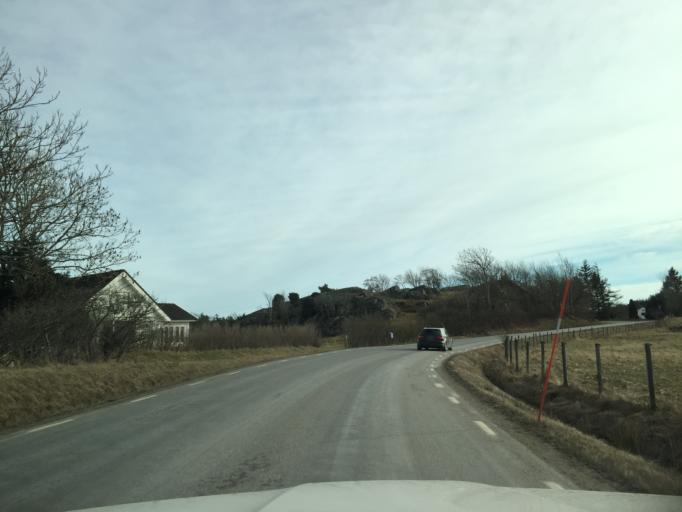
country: SE
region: Vaestra Goetaland
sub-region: Tjorns Kommun
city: Skaerhamn
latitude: 58.0290
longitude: 11.6038
